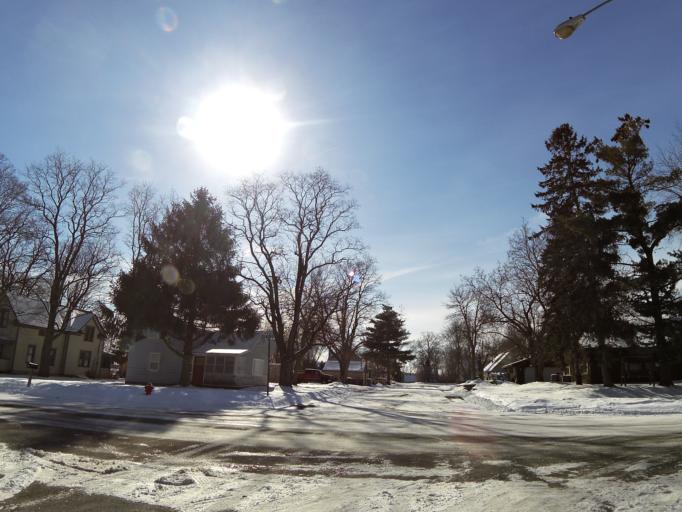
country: US
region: Minnesota
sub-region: Dakota County
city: Hastings
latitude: 44.7445
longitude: -92.8397
